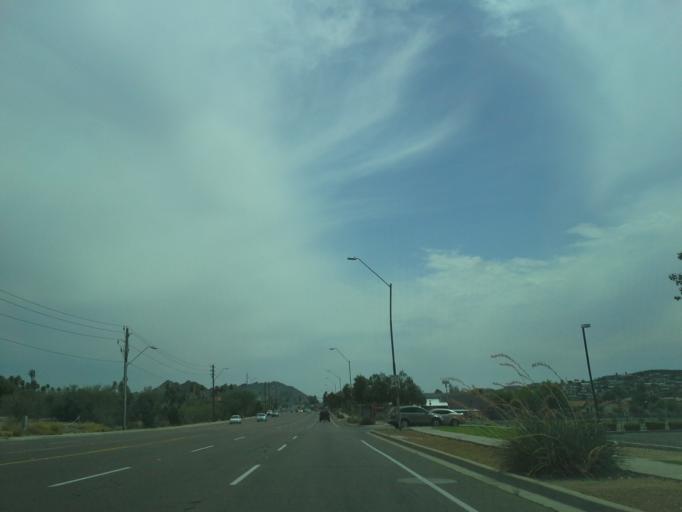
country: US
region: Arizona
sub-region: Maricopa County
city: Paradise Valley
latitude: 33.6147
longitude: -112.0348
